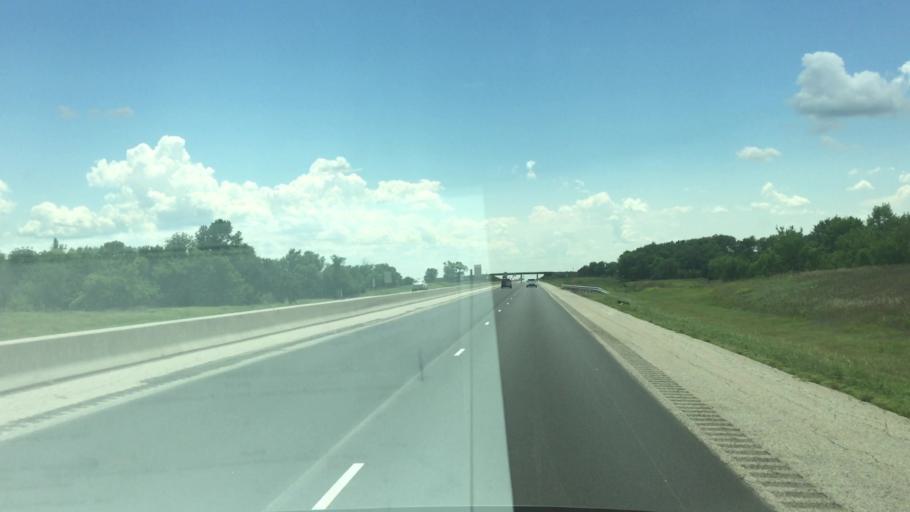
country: US
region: Kansas
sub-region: Osage County
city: Osage City
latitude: 38.7017
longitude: -95.9885
